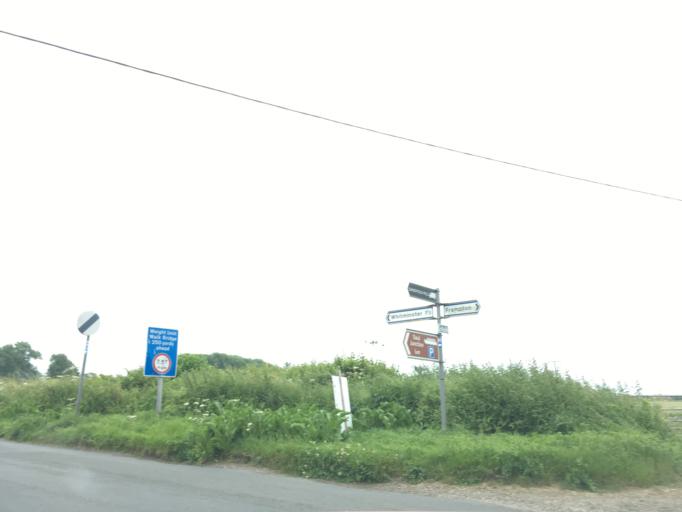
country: GB
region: England
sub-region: Gloucestershire
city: Stonehouse
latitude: 51.7776
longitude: -2.3553
